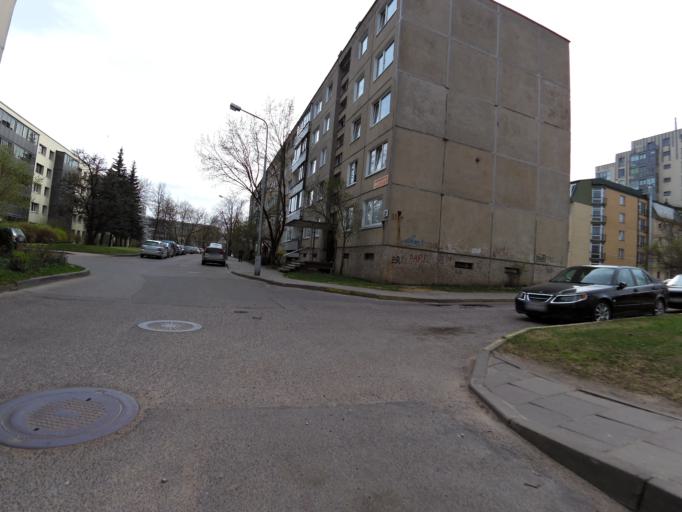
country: LT
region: Vilnius County
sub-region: Vilnius
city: Vilnius
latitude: 54.7019
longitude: 25.3008
